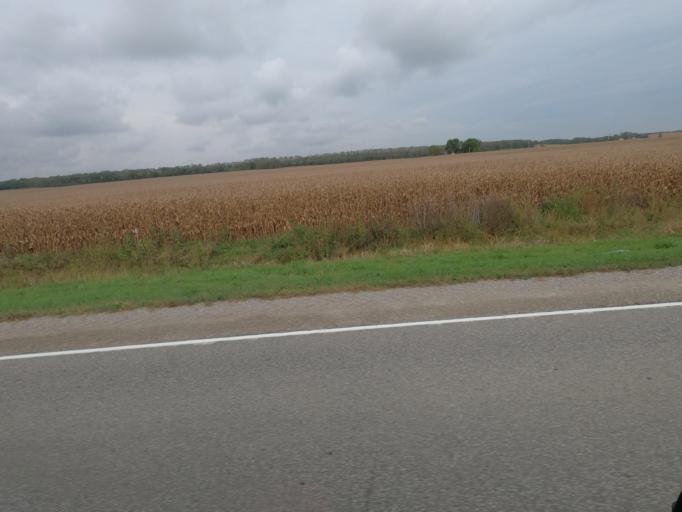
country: US
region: Iowa
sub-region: Wapello County
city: Ottumwa
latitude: 40.9080
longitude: -92.2069
